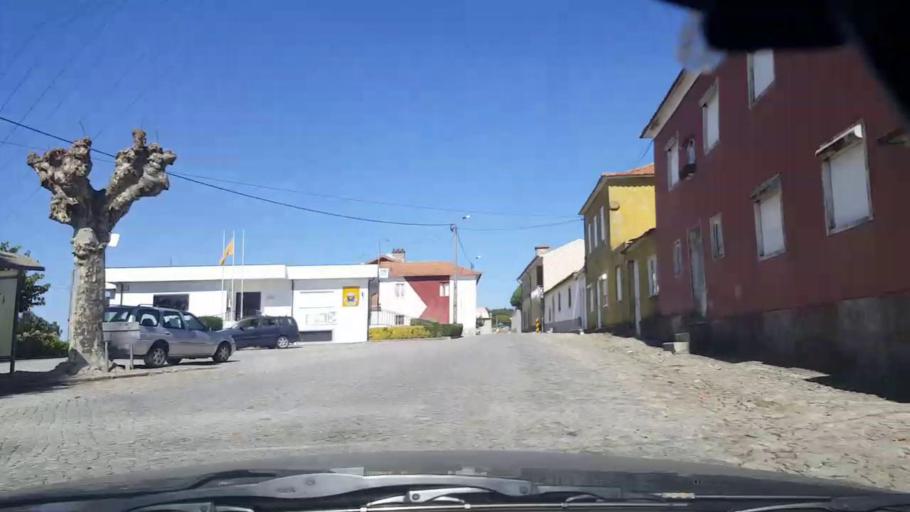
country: PT
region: Porto
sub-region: Vila do Conde
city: Arvore
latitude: 41.3375
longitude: -8.7177
